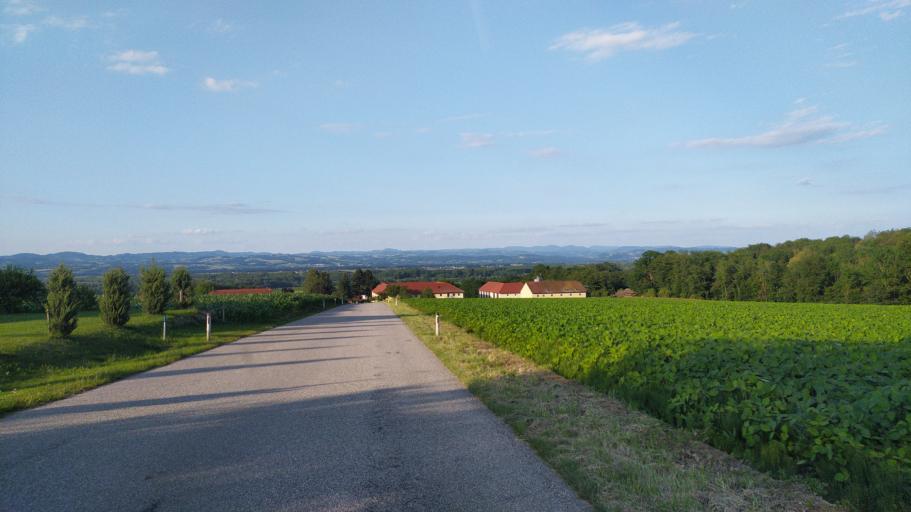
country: AT
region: Lower Austria
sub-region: Politischer Bezirk Amstetten
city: Strengberg
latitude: 48.1652
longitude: 14.6194
